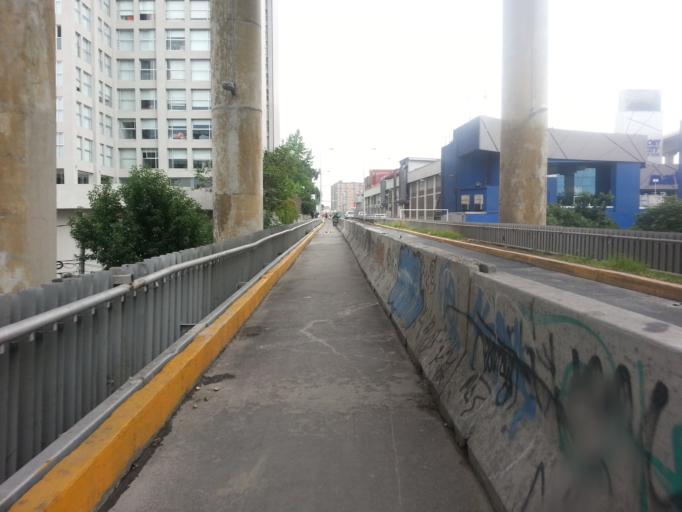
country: MX
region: Mexico City
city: Alvaro Obregon
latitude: 19.3848
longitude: -99.1918
